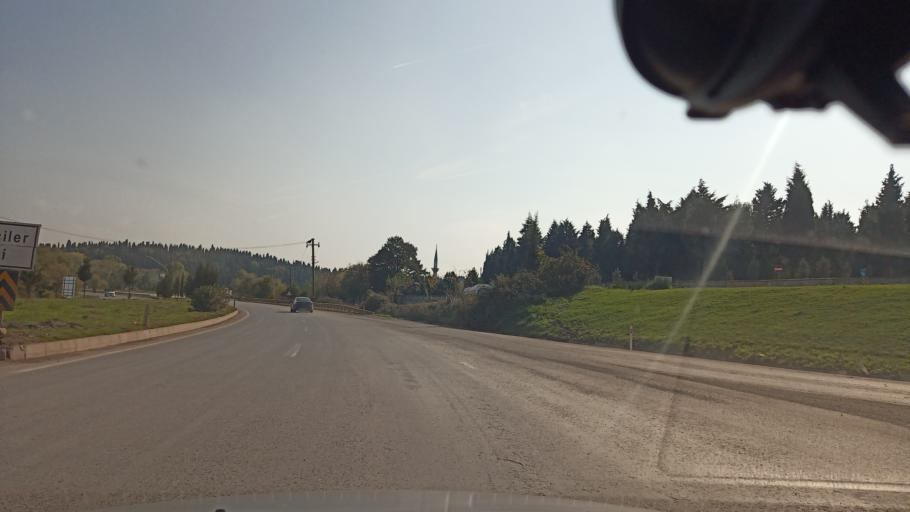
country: TR
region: Sakarya
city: Adapazari
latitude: 40.8296
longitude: 30.3796
